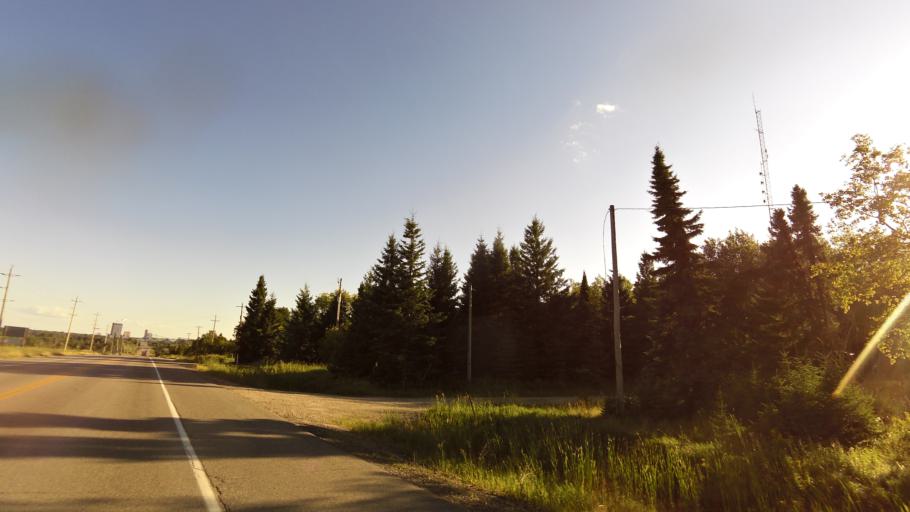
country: CA
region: Ontario
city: Dryden
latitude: 49.8114
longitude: -92.8474
